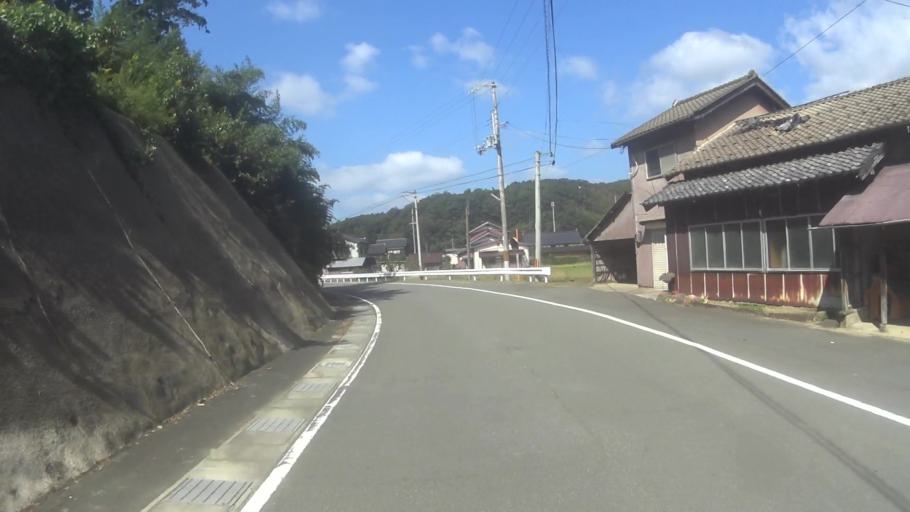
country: JP
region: Kyoto
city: Miyazu
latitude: 35.7126
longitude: 135.1149
